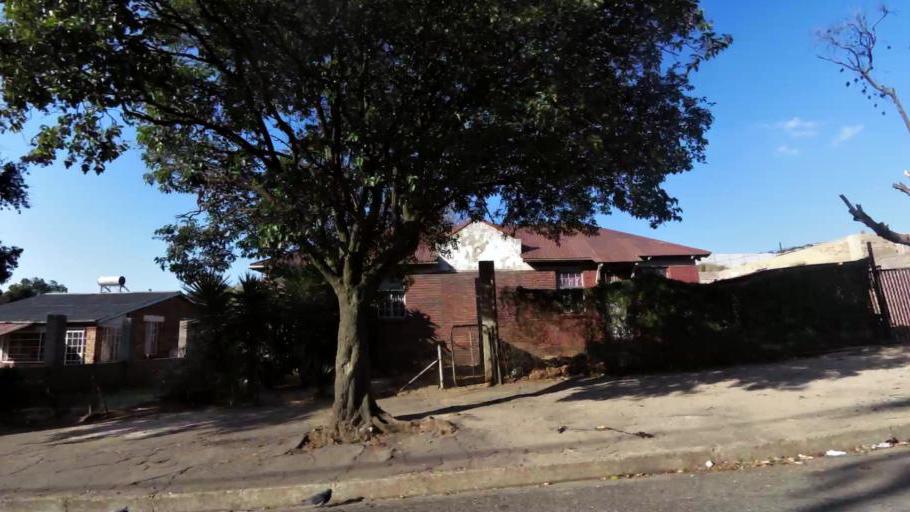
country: ZA
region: Gauteng
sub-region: City of Johannesburg Metropolitan Municipality
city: Johannesburg
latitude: -26.1906
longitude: 28.0155
